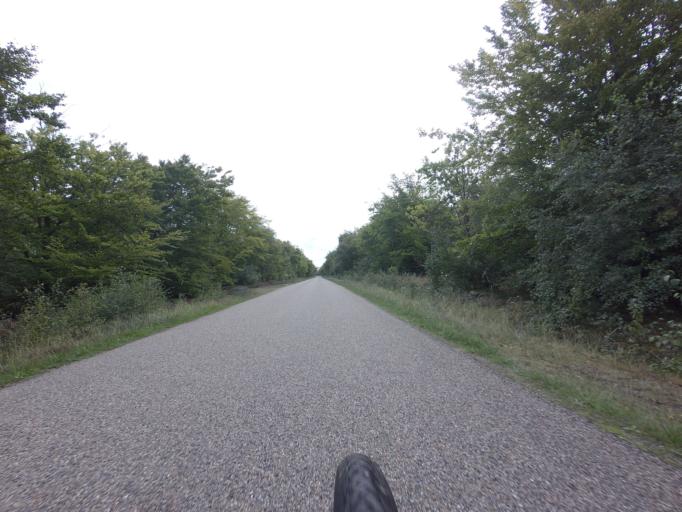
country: DK
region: North Denmark
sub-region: Hjorring Kommune
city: Hirtshals
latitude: 57.5798
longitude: 10.0330
